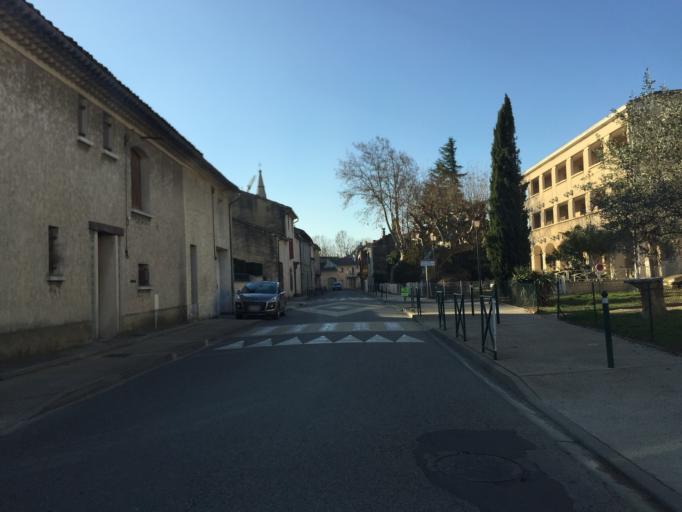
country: FR
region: Provence-Alpes-Cote d'Azur
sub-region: Departement du Vaucluse
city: Sainte-Cecile-les-Vignes
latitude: 44.2453
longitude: 4.8896
